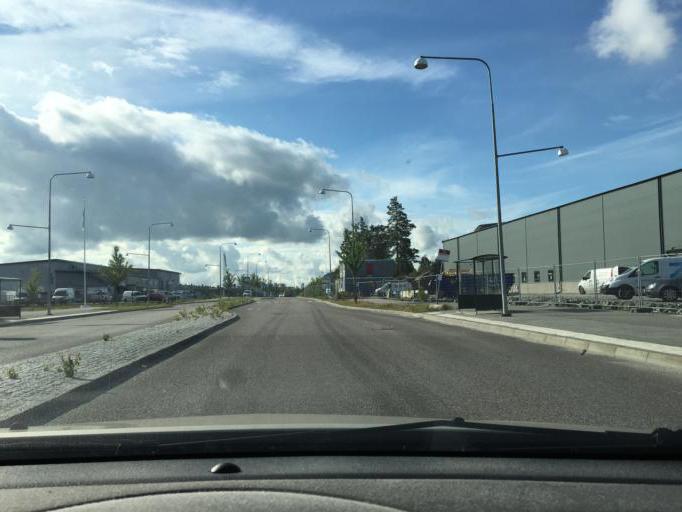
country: SE
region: Stockholm
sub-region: Sodertalje Kommun
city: Soedertaelje
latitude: 59.2073
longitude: 17.6617
